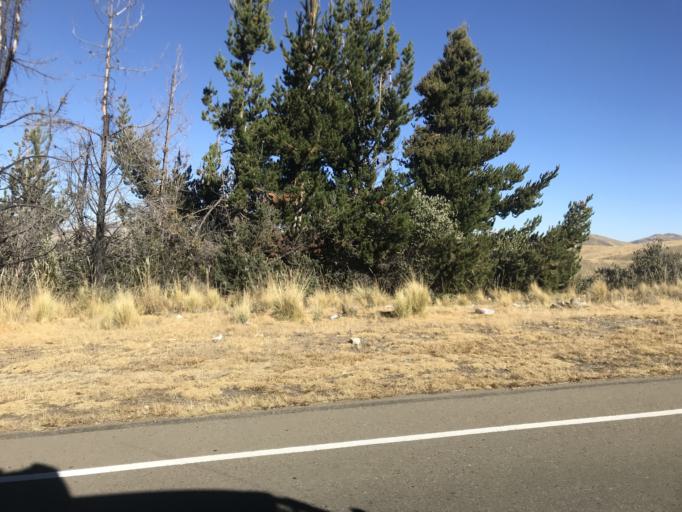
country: PE
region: Puno
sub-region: Yunguyo
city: Yunguyo
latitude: -16.1725
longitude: -68.9828
